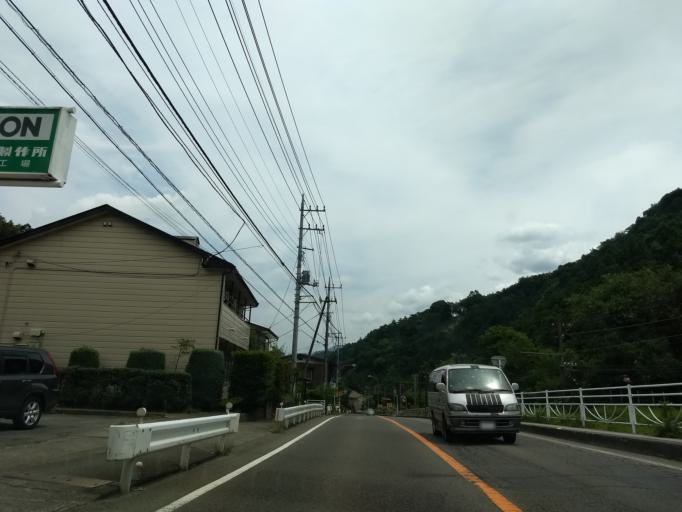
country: JP
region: Yamanashi
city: Otsuki
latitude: 35.5389
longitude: 138.8835
